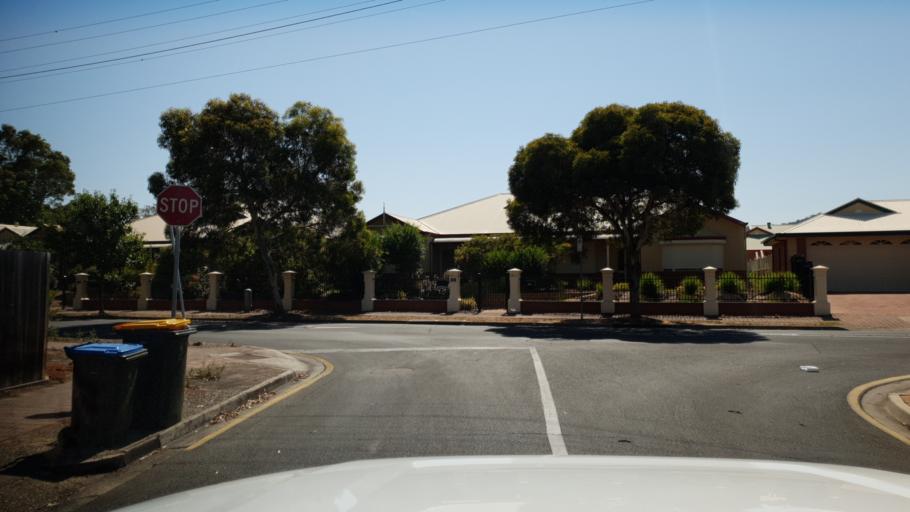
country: AU
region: South Australia
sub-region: Marion
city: Clovelly Park
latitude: -34.9944
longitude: 138.5820
